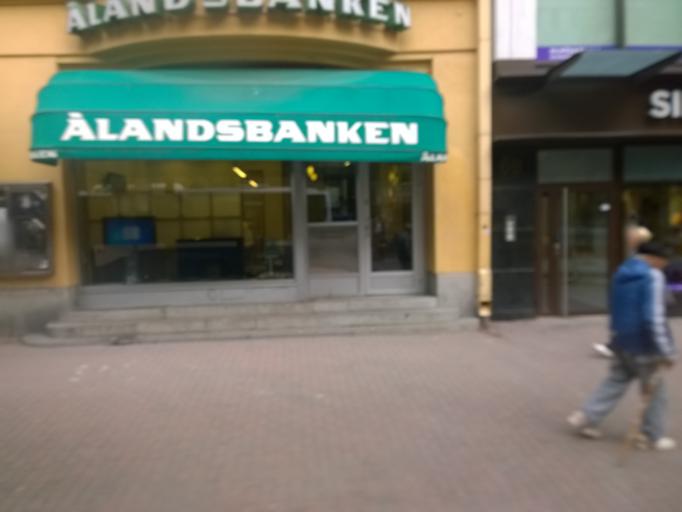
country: FI
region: Pirkanmaa
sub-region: Tampere
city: Tampere
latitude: 61.4984
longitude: 23.7691
